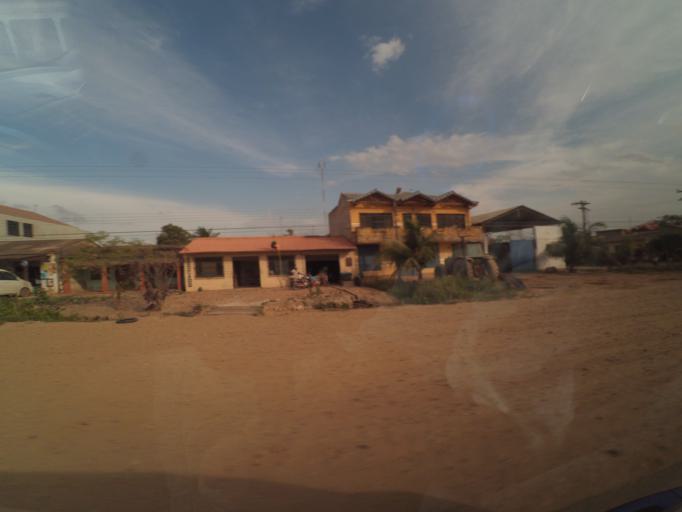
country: BO
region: Santa Cruz
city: Okinawa Numero Uno
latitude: -17.2208
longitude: -62.8978
